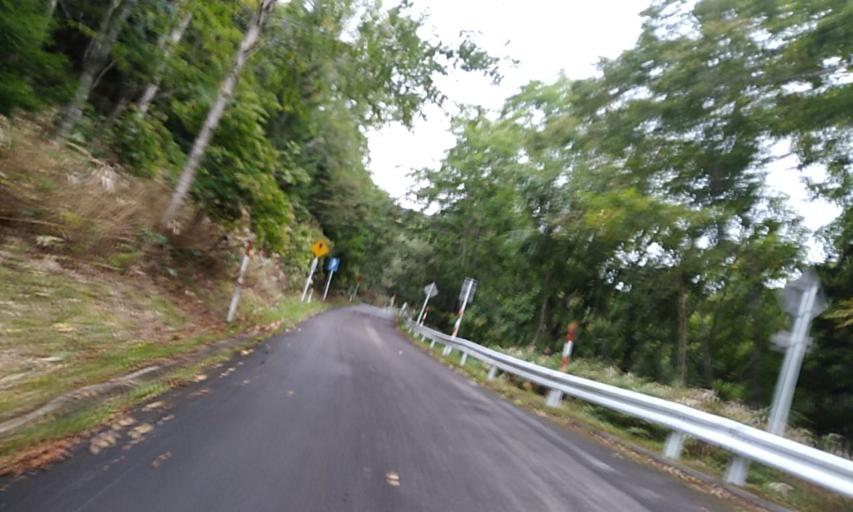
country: JP
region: Hokkaido
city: Bihoro
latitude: 43.5664
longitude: 144.1913
